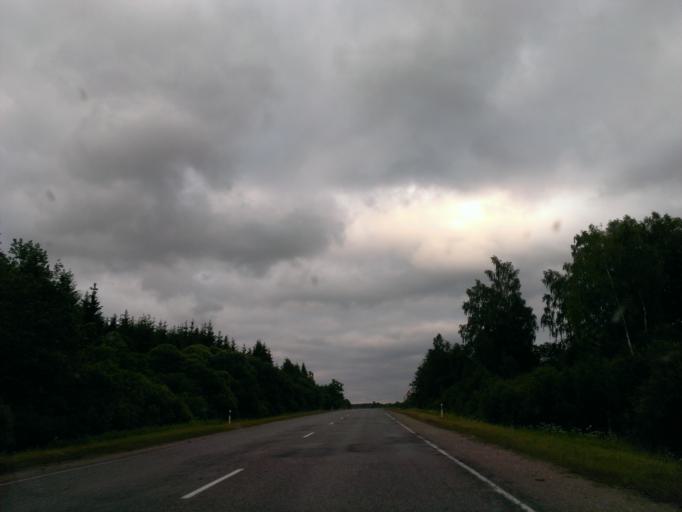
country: LV
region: Saldus Rajons
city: Saldus
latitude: 56.6702
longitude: 22.3987
